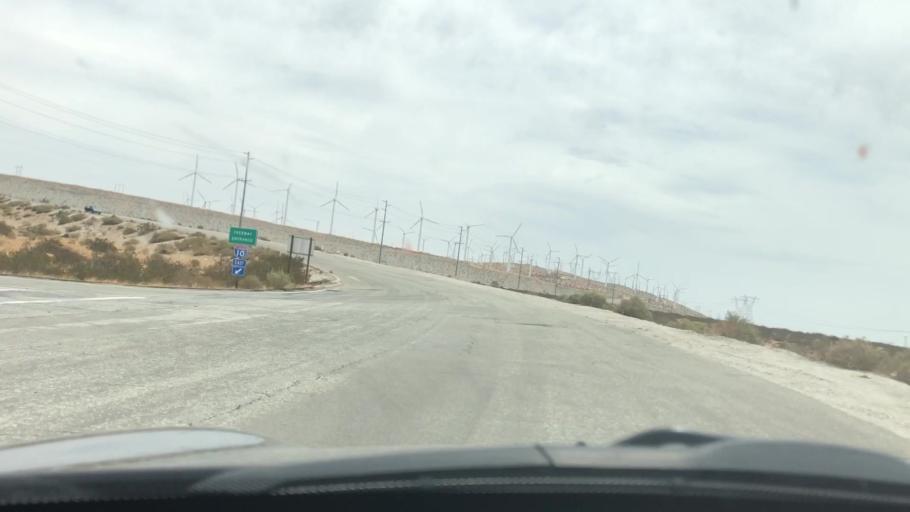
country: US
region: California
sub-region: Riverside County
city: Garnet
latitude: 33.9213
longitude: -116.6475
